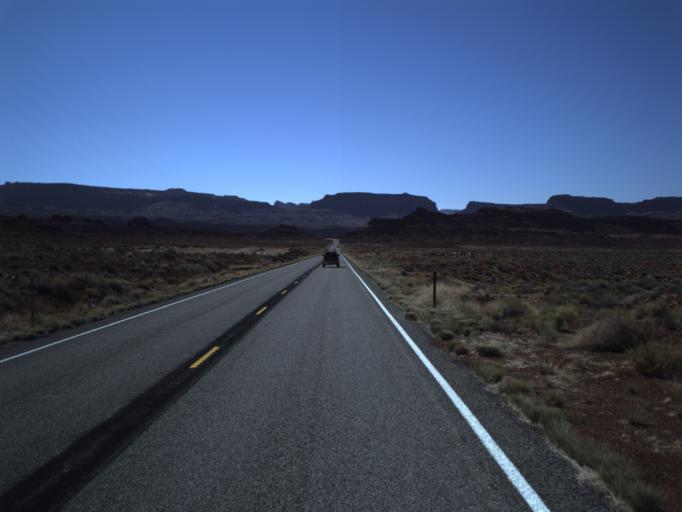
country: US
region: Utah
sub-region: San Juan County
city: Blanding
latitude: 37.8449
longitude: -110.3551
